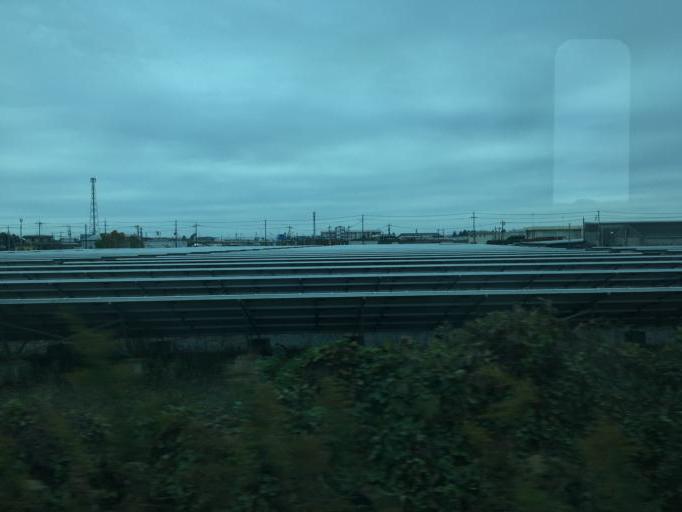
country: JP
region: Ibaraki
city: Yuki
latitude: 36.2965
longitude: 139.9007
